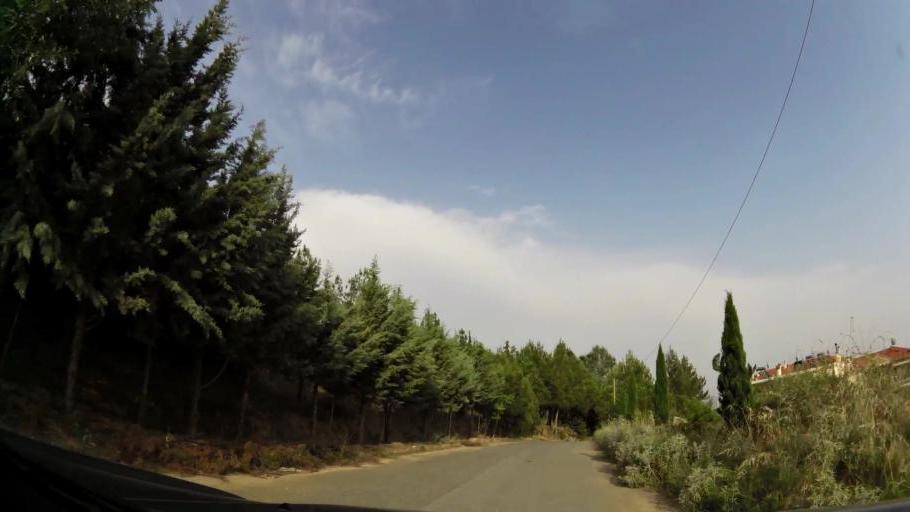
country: GR
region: Central Macedonia
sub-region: Nomos Thessalonikis
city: Oraiokastro
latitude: 40.7259
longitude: 22.9050
